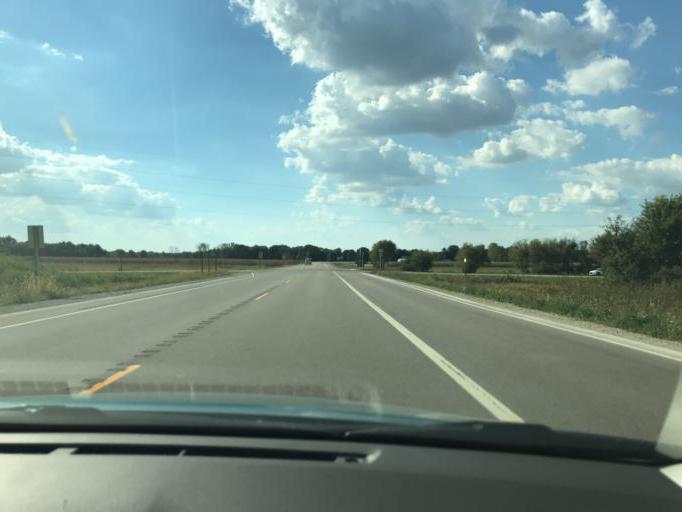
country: US
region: Wisconsin
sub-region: Green County
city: Brodhead
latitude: 42.5744
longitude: -89.3651
